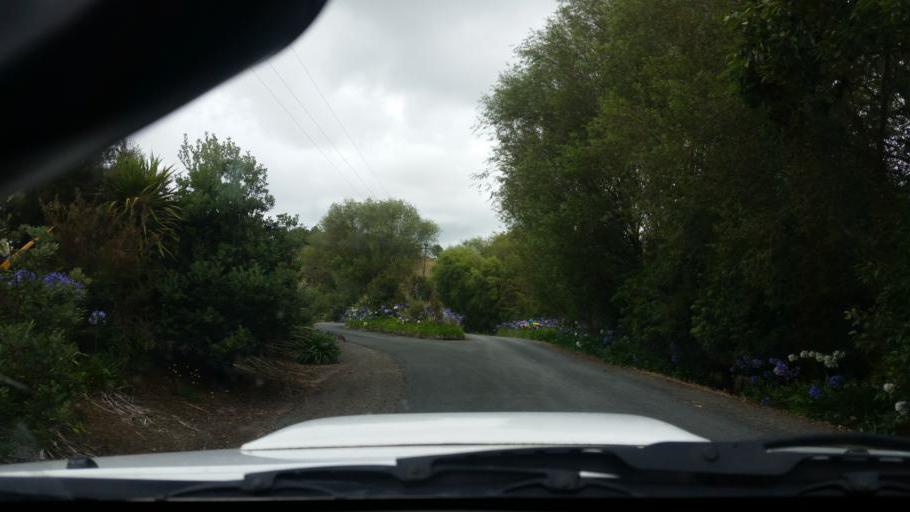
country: NZ
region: Northland
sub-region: Whangarei
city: Ruakaka
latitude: -36.0957
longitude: 174.3539
